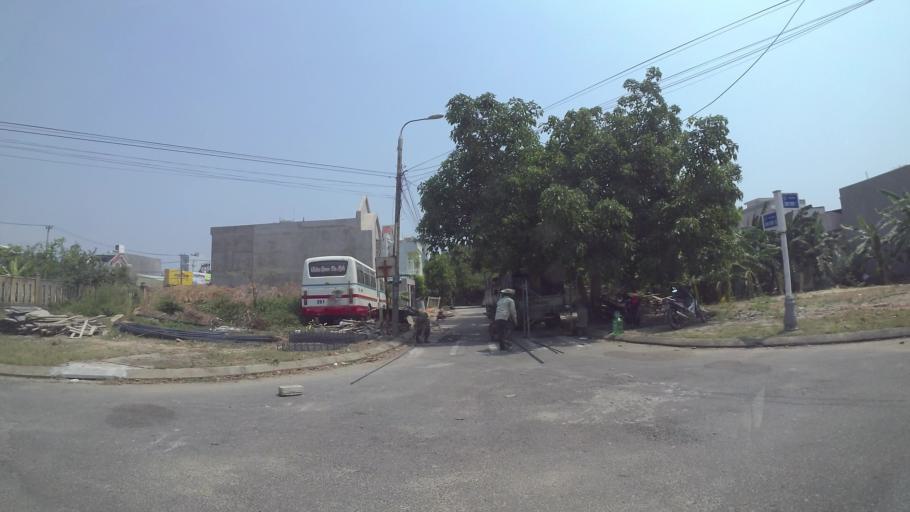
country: VN
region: Da Nang
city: Ngu Hanh Son
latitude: 16.0137
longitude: 108.2543
